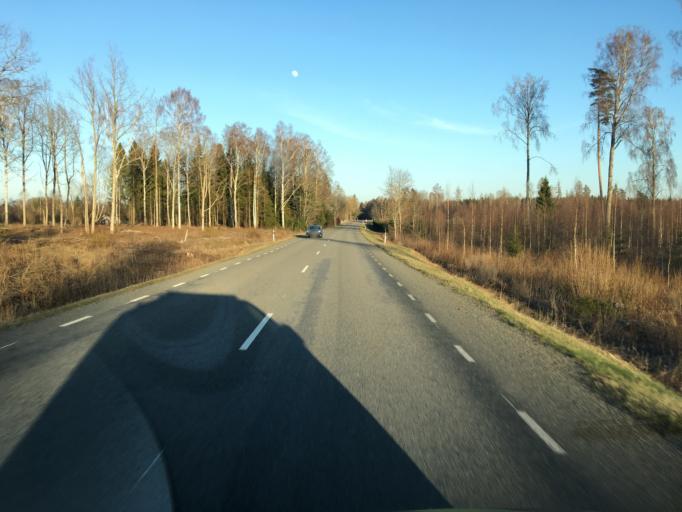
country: EE
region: Raplamaa
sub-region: Rapla vald
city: Rapla
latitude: 59.0698
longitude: 24.9089
